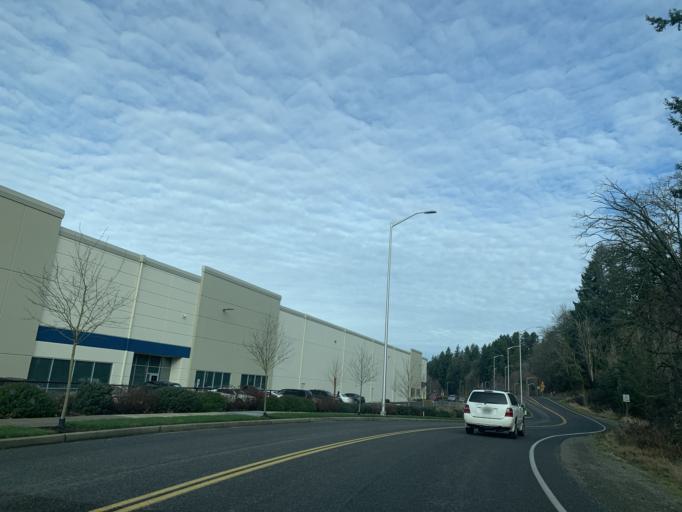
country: US
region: Washington
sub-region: Pierce County
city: Milton
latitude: 47.2321
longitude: -122.3239
